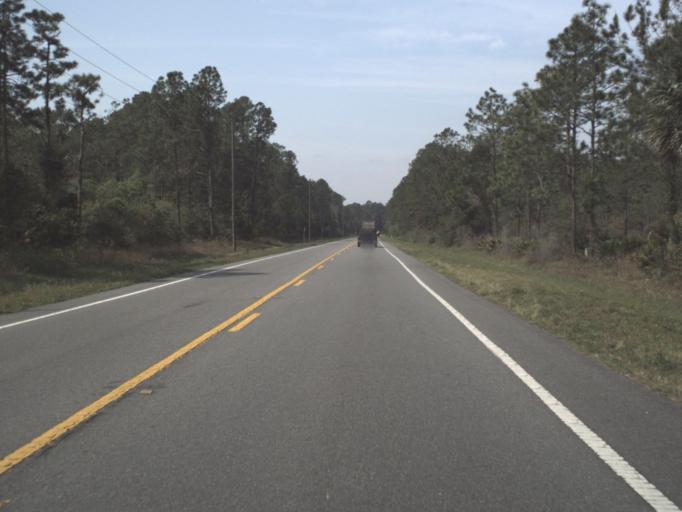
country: US
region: Florida
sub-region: Lake County
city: Astor
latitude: 29.1611
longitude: -81.5526
